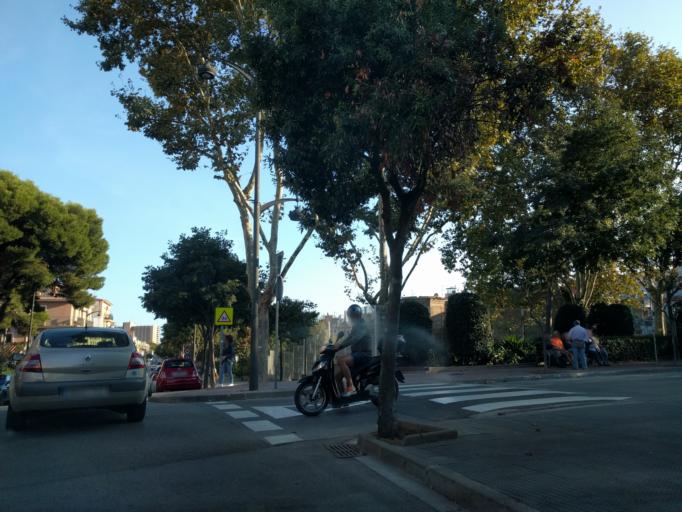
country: ES
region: Catalonia
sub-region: Provincia de Girona
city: Sant Feliu de Guixols
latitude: 41.7869
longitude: 3.0316
